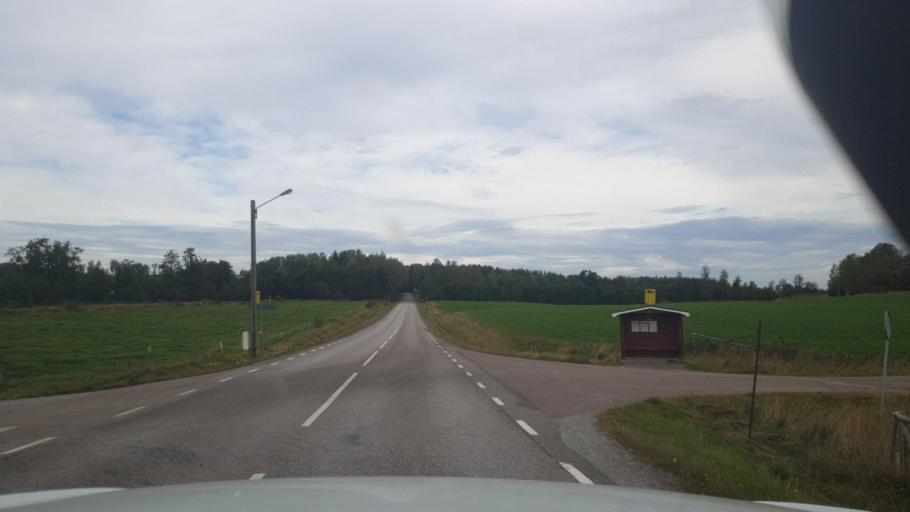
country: SE
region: Vaermland
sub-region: Arvika Kommun
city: Arvika
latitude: 59.5251
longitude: 12.6207
